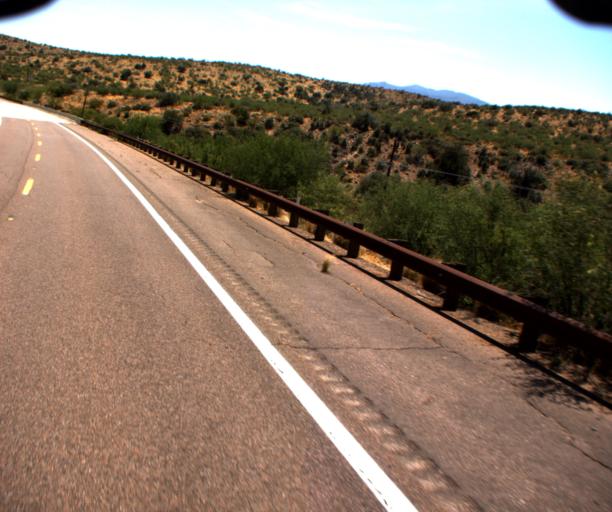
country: US
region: Arizona
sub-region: Gila County
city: Tonto Basin
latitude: 33.9950
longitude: -111.3151
